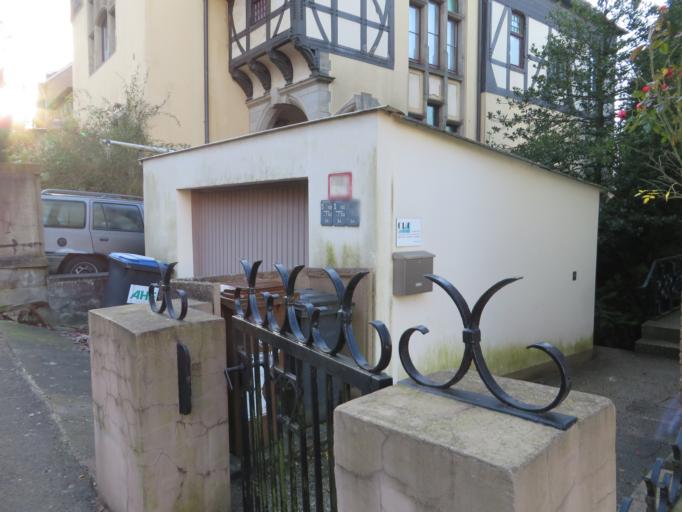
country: DE
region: North Rhine-Westphalia
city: Witten
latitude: 51.4323
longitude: 7.3399
